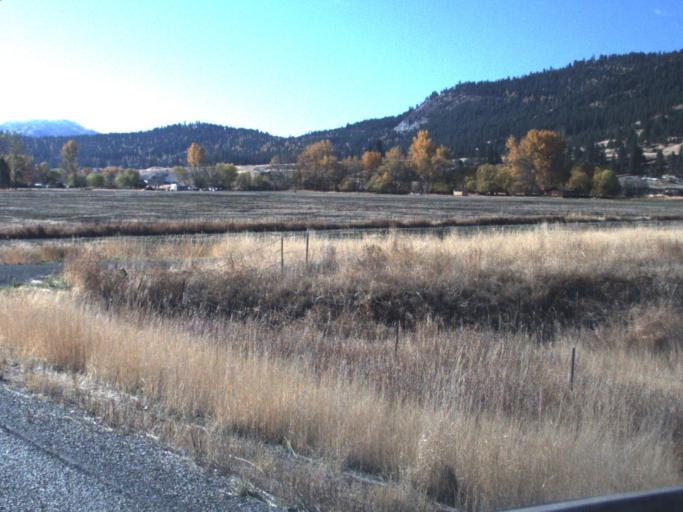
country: US
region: Washington
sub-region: Ferry County
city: Republic
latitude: 48.6850
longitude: -118.6625
